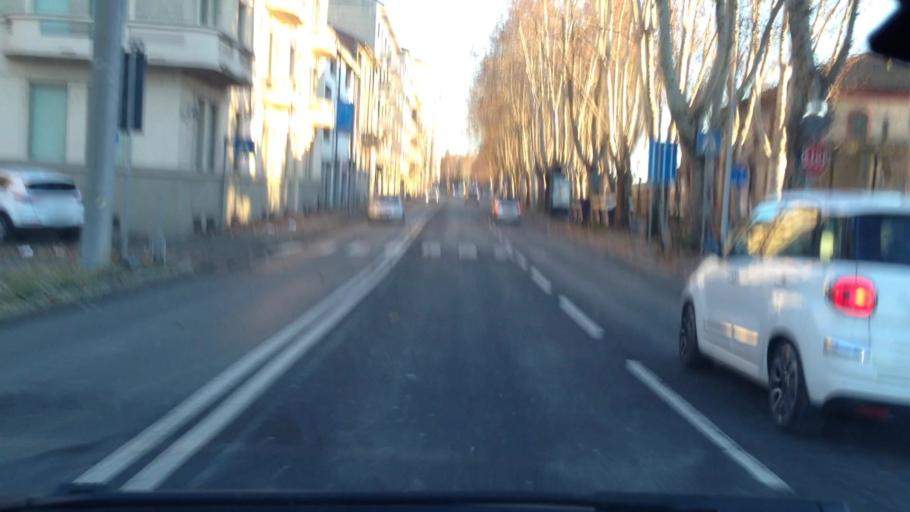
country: IT
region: Piedmont
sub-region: Provincia di Alessandria
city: Alessandria
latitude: 44.9136
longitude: 8.6031
